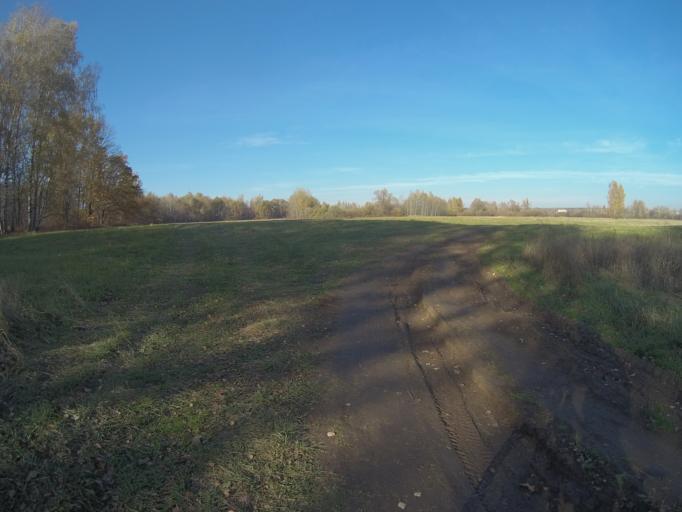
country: RU
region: Vladimir
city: Orgtrud
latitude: 56.1703
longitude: 40.5904
